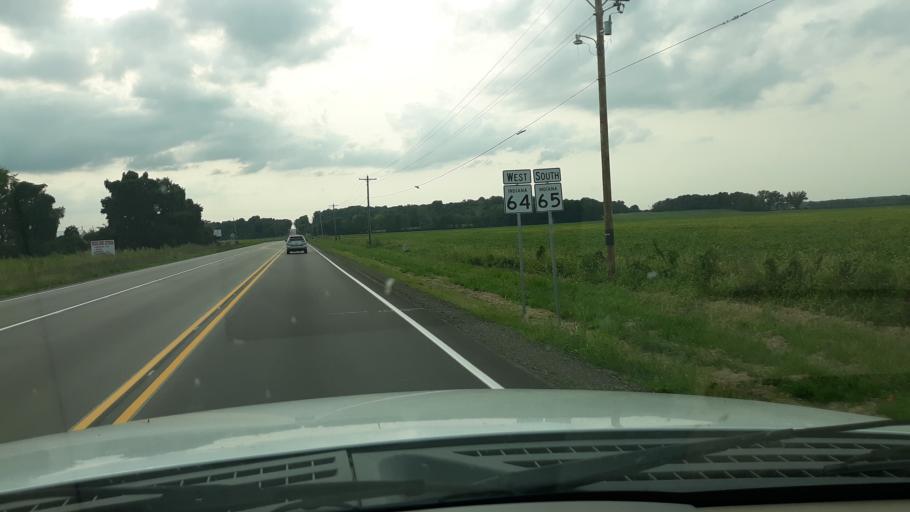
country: US
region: Indiana
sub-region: Gibson County
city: Princeton
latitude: 38.3558
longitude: -87.6414
